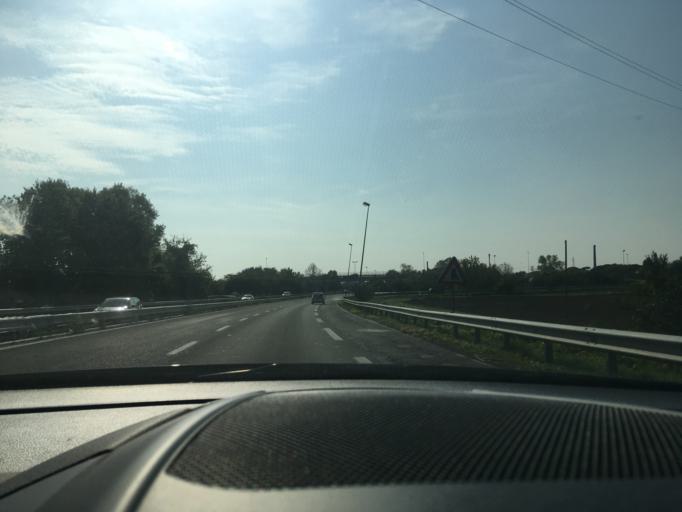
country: IT
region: Emilia-Romagna
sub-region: Provincia di Rimini
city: Bellaria-Igea Marina
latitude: 44.1439
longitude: 12.4553
